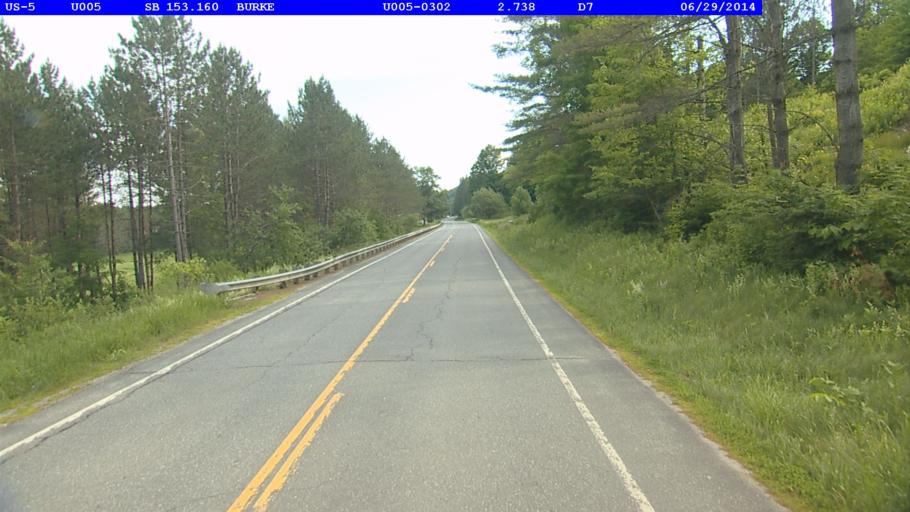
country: US
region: Vermont
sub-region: Caledonia County
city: Lyndonville
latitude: 44.6241
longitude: -71.9706
